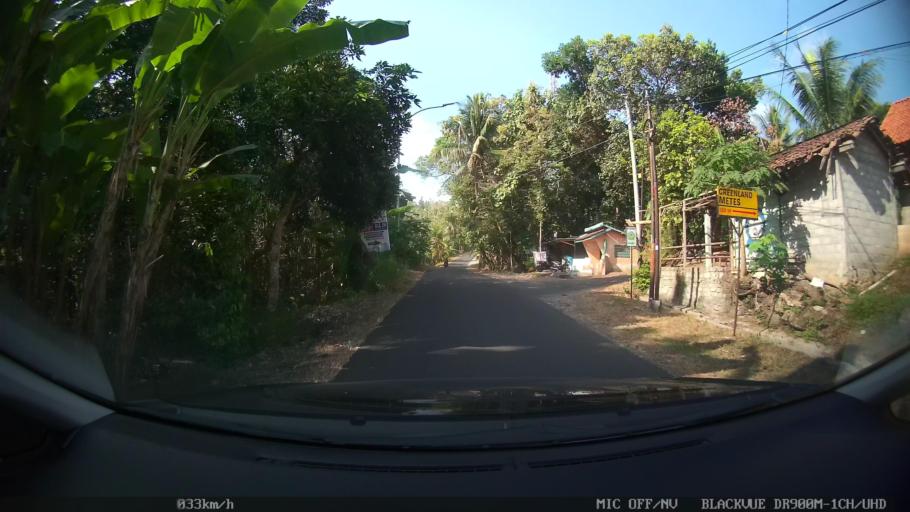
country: ID
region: Daerah Istimewa Yogyakarta
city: Kasihan
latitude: -7.8308
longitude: 110.2737
